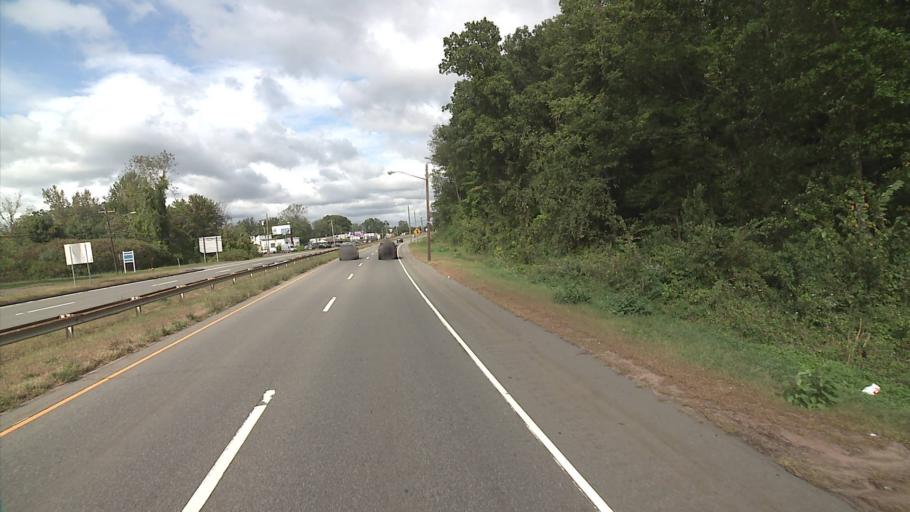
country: US
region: Connecticut
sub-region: New Haven County
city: Meriden
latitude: 41.5597
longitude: -72.7759
